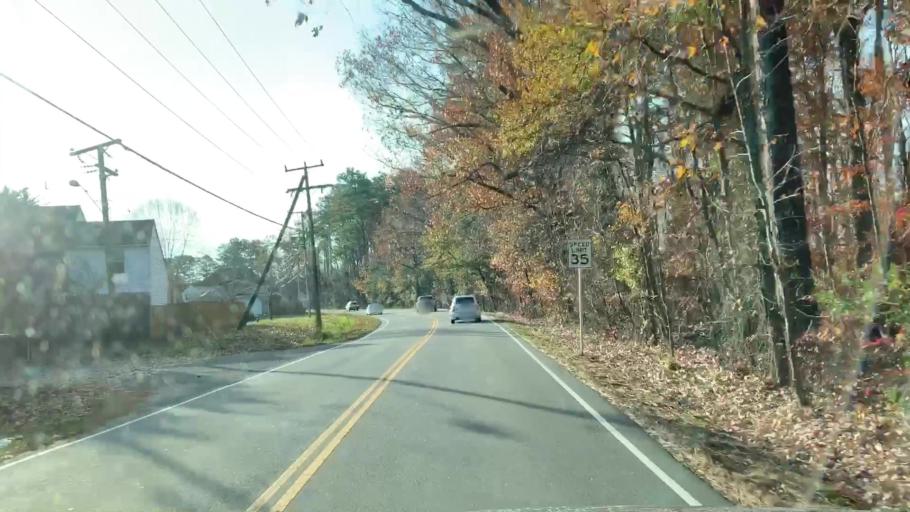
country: US
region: Virginia
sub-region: City of Chesapeake
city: Chesapeake
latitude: 36.7647
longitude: -76.1492
